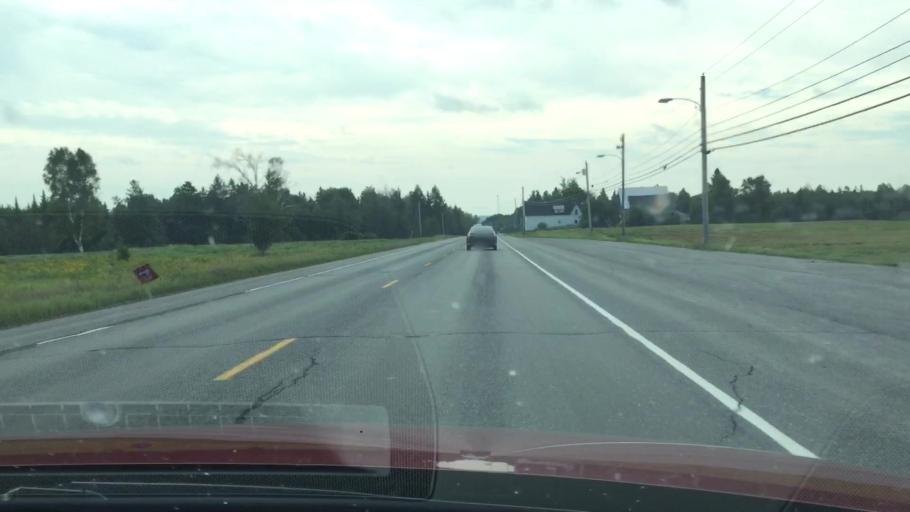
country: US
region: Maine
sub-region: Aroostook County
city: Houlton
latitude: 46.1800
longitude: -67.8411
